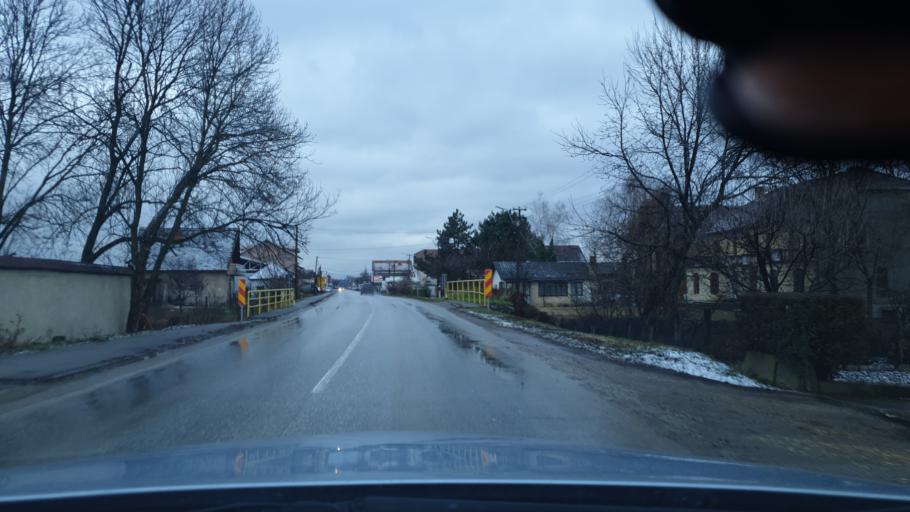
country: RS
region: Central Serbia
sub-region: Branicevski Okrug
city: Petrovac
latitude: 44.3899
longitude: 21.4080
